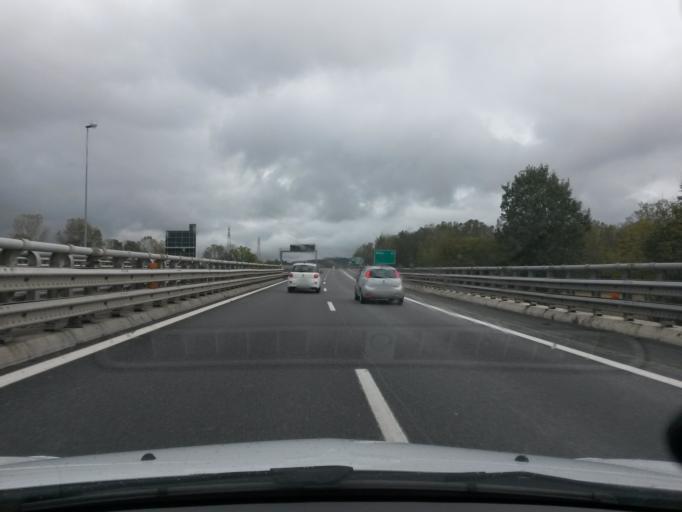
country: IT
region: Piedmont
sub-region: Provincia di Torino
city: Drubiaglio-Grangia
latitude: 45.0908
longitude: 7.4232
